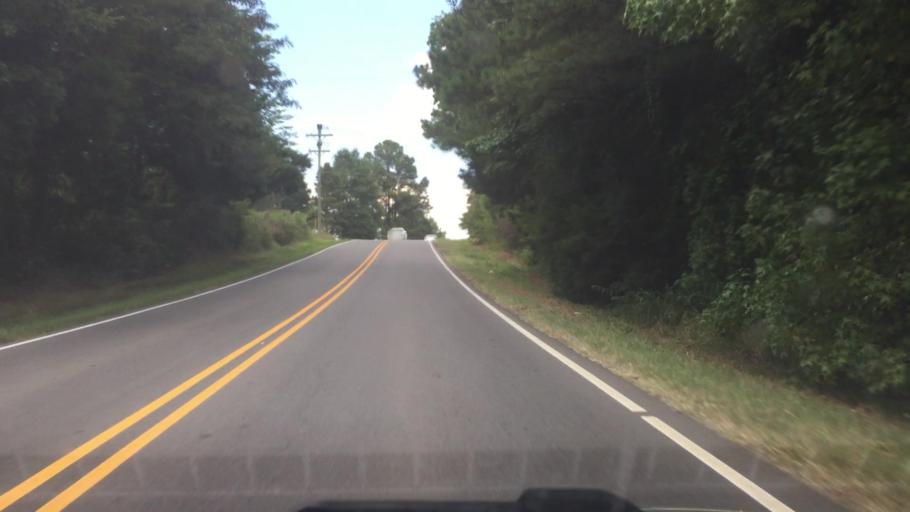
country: US
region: North Carolina
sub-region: Mecklenburg County
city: Huntersville
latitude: 35.4115
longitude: -80.7538
